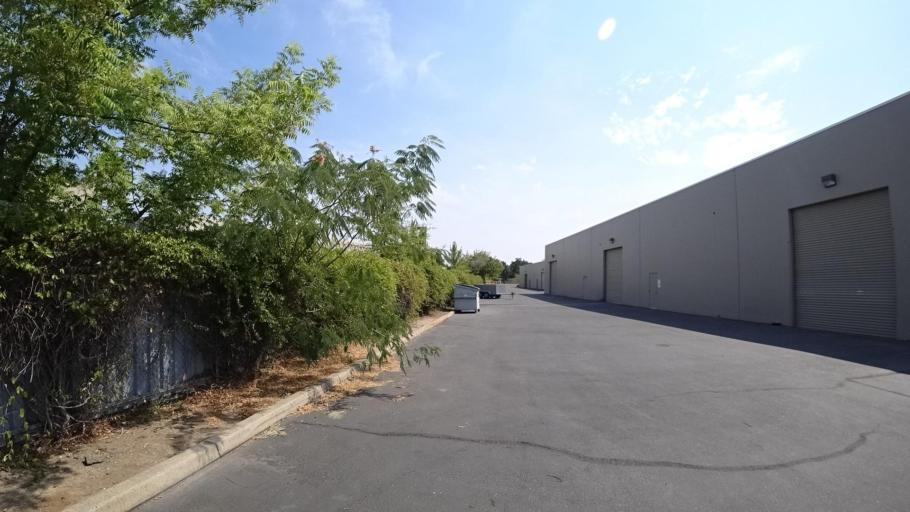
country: US
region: California
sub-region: Placer County
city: Rocklin
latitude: 38.7979
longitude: -121.2304
